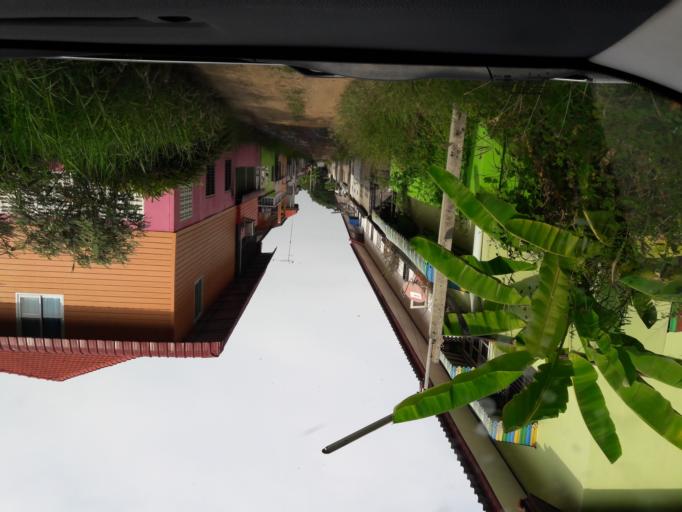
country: TH
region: Ang Thong
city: Ang Thong
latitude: 14.5852
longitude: 100.4442
